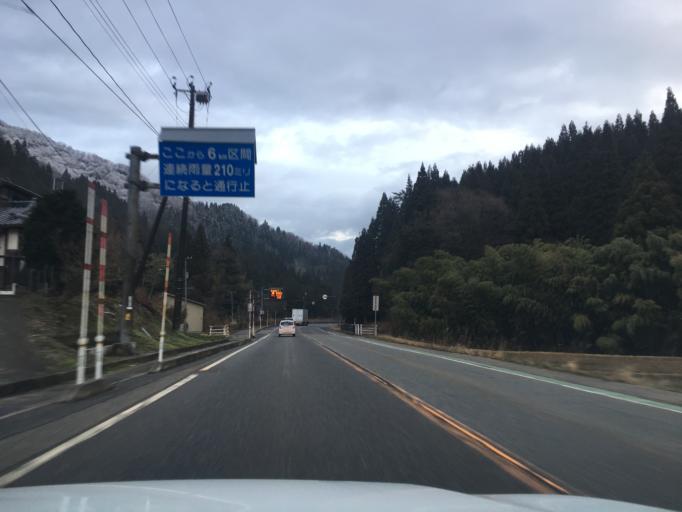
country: JP
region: Niigata
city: Murakami
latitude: 38.3905
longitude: 139.5550
